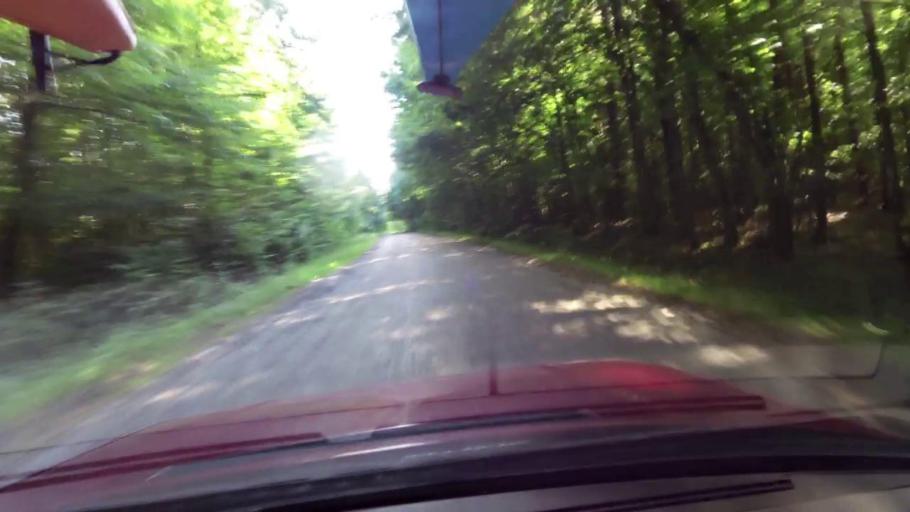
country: PL
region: Pomeranian Voivodeship
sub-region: Powiat slupski
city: Kepice
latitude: 54.1601
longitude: 16.9074
